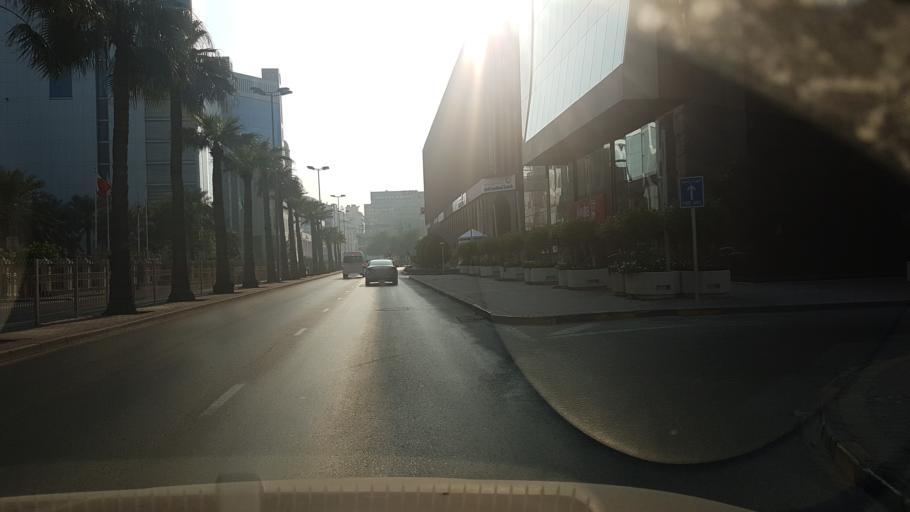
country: BH
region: Manama
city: Manama
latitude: 26.2360
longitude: 50.5776
